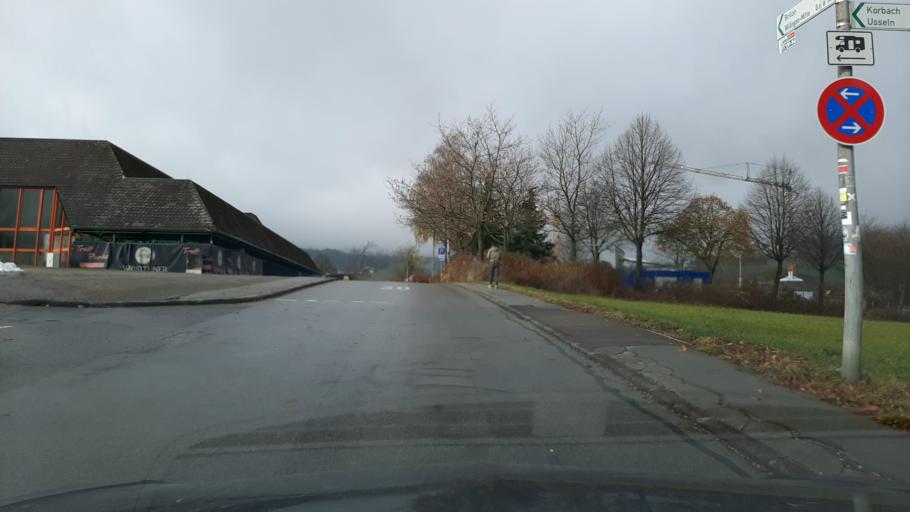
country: DE
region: Hesse
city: Willingen
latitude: 51.2899
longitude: 8.6136
